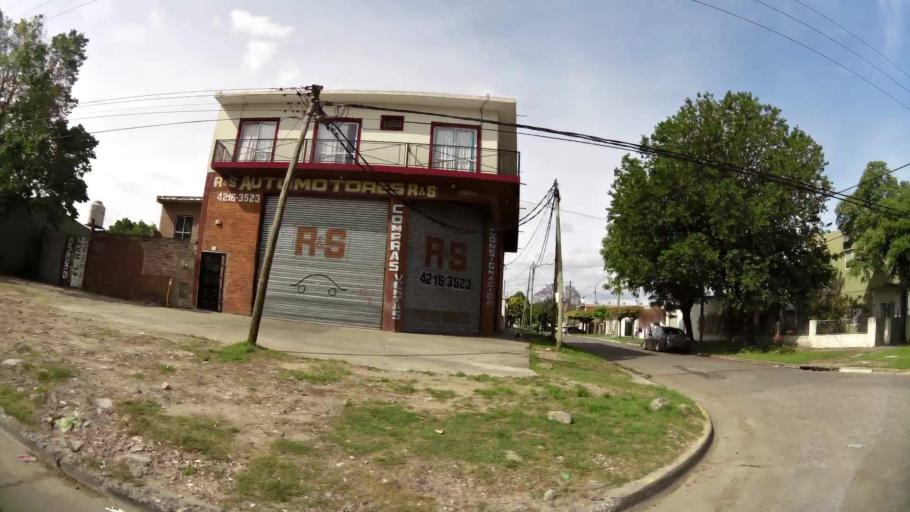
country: AR
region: Buenos Aires
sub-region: Partido de Quilmes
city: Quilmes
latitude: -34.7715
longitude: -58.2432
